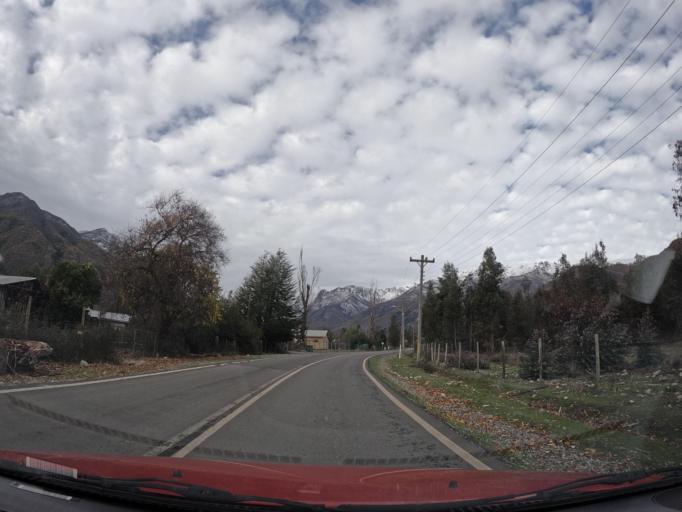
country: CL
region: Maule
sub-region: Provincia de Linares
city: Colbun
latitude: -35.8605
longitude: -71.2609
